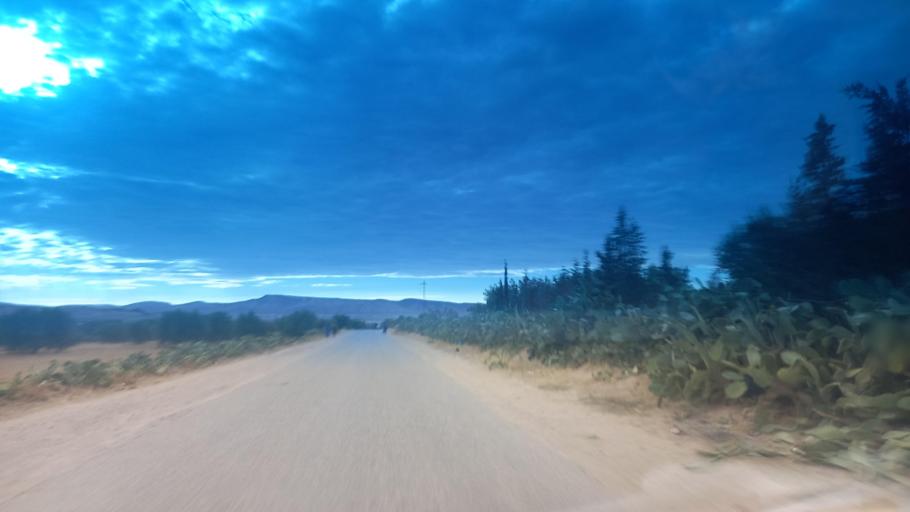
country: TN
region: Al Qasrayn
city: Sbiba
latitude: 35.3798
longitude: 9.0570
